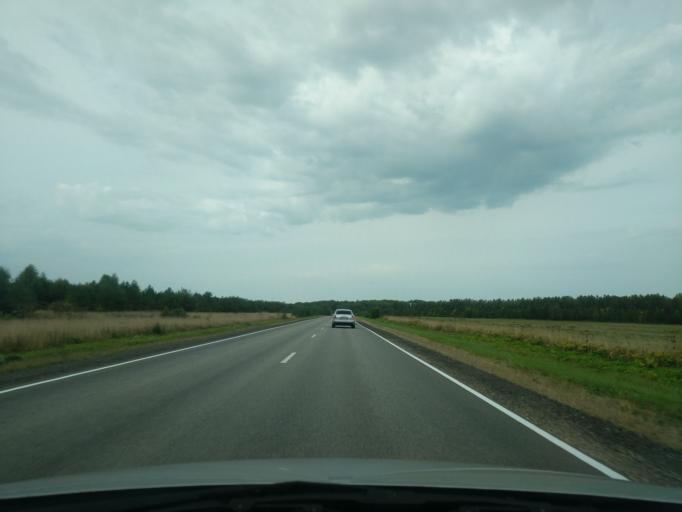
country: RU
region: Kirov
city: Mirnyy
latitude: 58.2734
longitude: 47.7669
